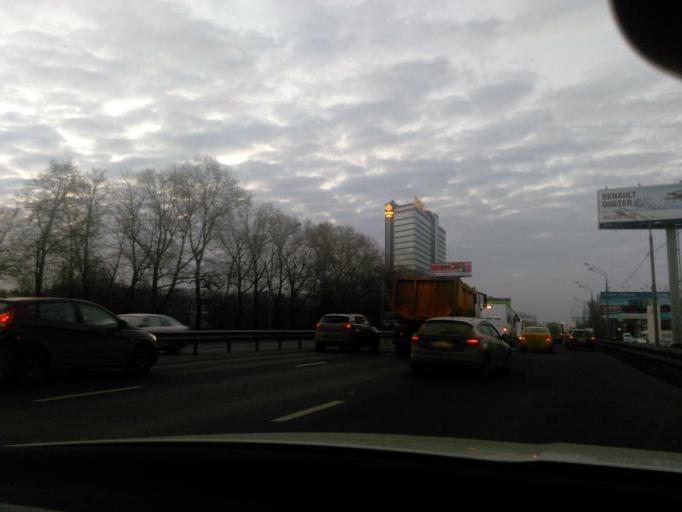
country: RU
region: Moscow
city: Khimki
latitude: 55.8976
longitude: 37.4248
